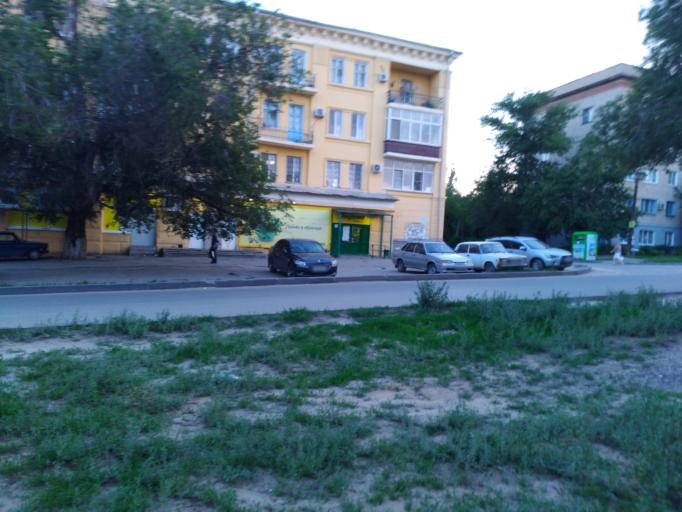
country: RU
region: Volgograd
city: Volgograd
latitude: 48.6722
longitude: 44.4488
